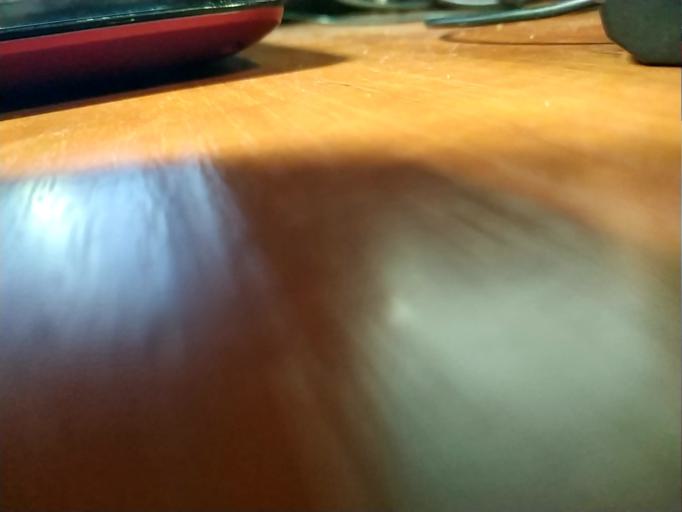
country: RU
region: Tverskaya
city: Likhoslavl'
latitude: 57.2225
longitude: 35.7106
